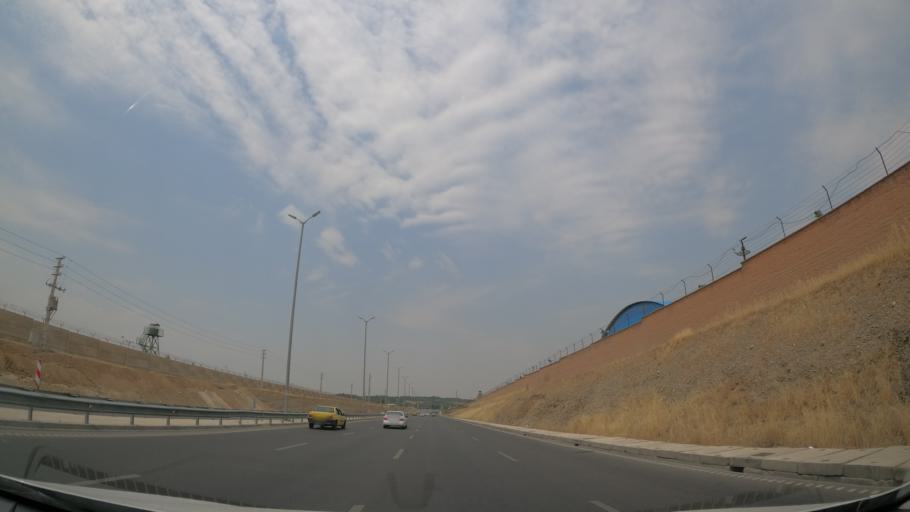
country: IR
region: Tehran
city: Shahr-e Qods
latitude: 35.7401
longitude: 51.2315
